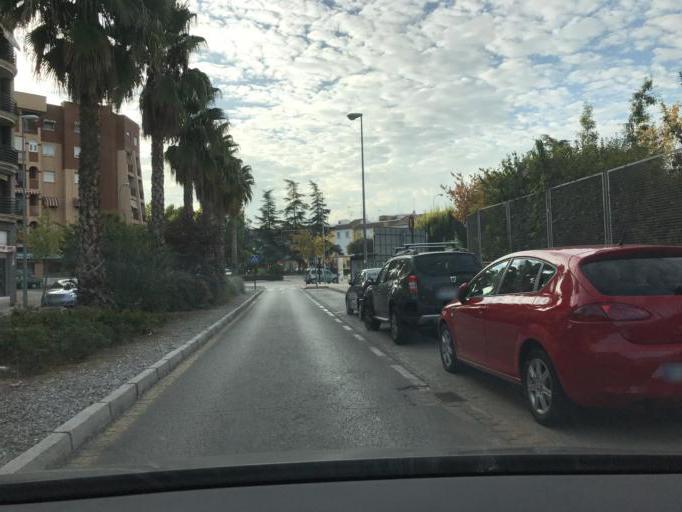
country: ES
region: Andalusia
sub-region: Provincia de Granada
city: Maracena
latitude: 37.1939
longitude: -3.6240
